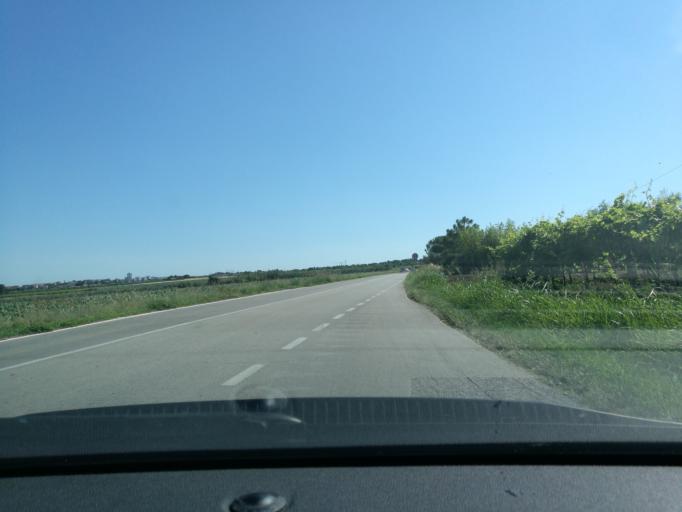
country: IT
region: Abruzzo
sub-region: Provincia di Chieti
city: Vasto
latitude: 42.1601
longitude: 14.7031
